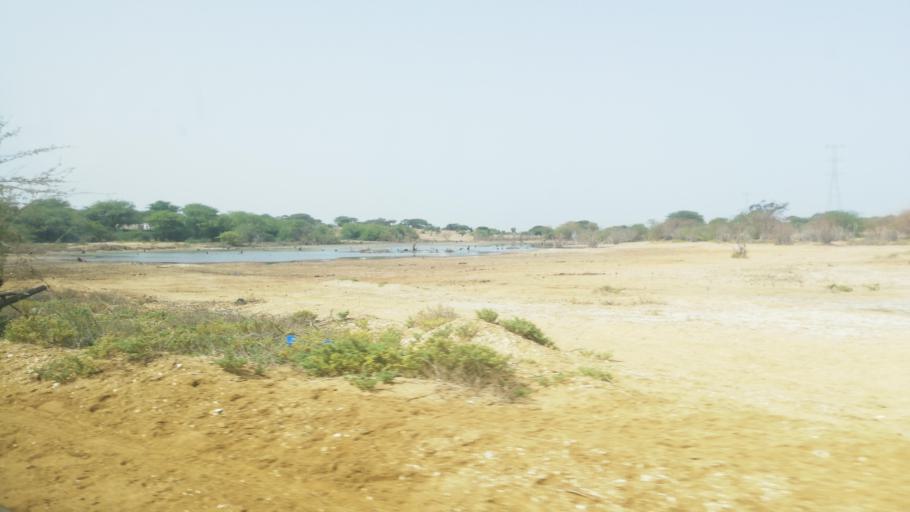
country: SN
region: Saint-Louis
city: Saint-Louis
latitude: 16.0794
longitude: -16.3606
